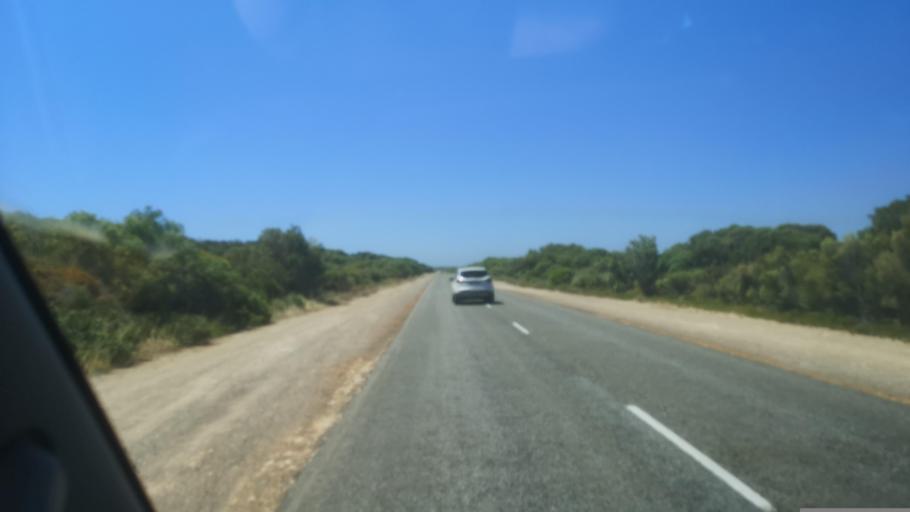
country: AU
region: Western Australia
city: Port Denison
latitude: -29.6293
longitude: 114.9702
